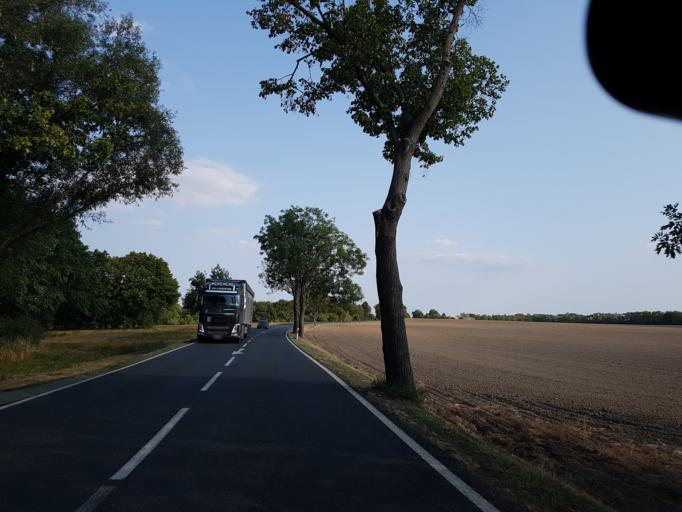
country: DE
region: Saxony
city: Elsnig
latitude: 51.6029
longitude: 12.9384
